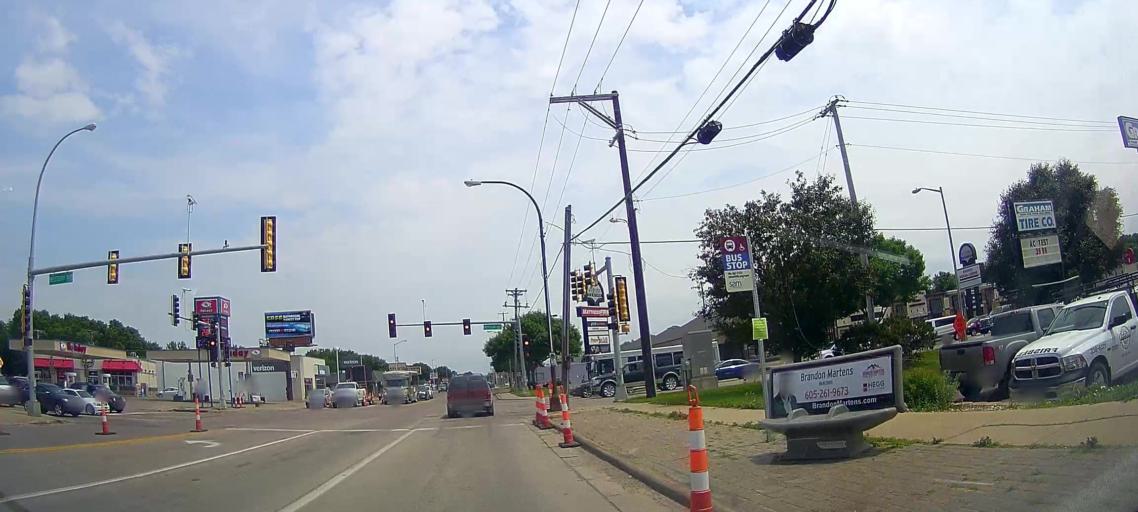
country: US
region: South Dakota
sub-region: Minnehaha County
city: Sioux Falls
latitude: 43.5148
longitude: -96.7515
